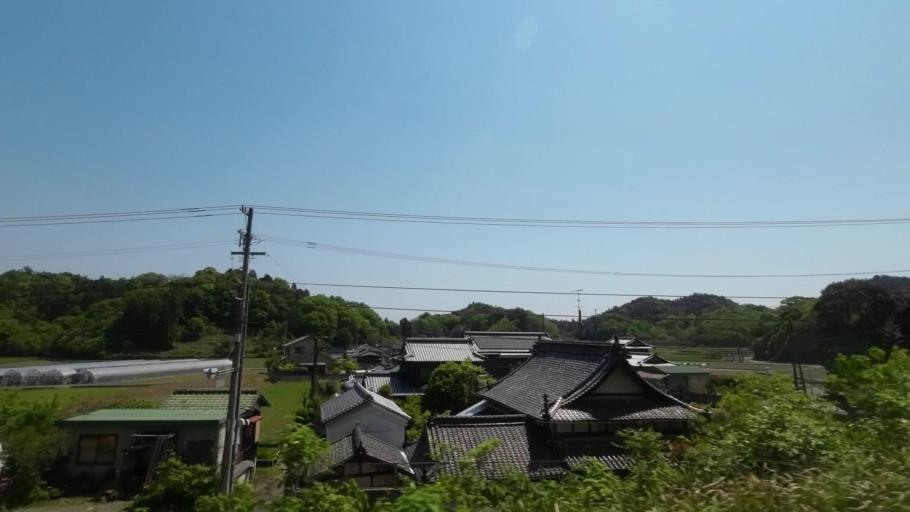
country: JP
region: Ehime
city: Saijo
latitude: 33.9898
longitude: 133.0521
